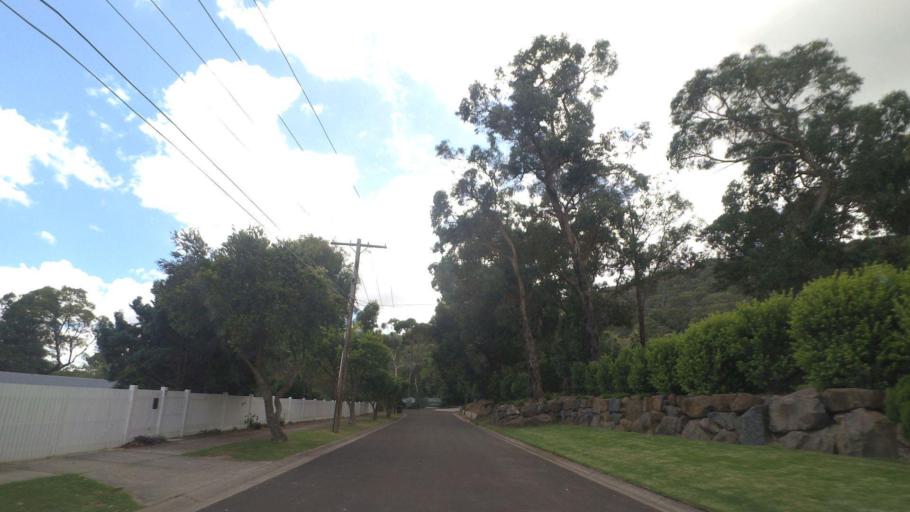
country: AU
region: Victoria
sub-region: Knox
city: Ferntree Gully
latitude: -37.8733
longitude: 145.3047
